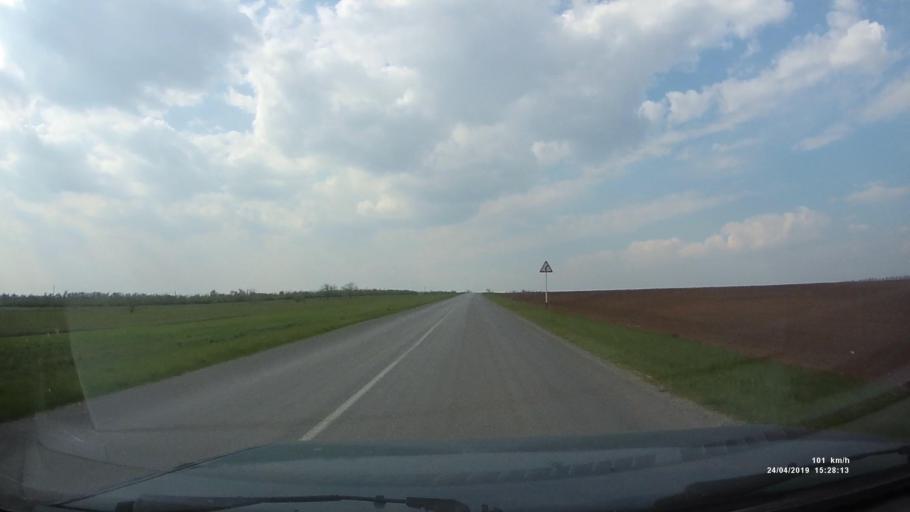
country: RU
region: Rostov
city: Remontnoye
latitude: 46.5761
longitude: 43.0197
